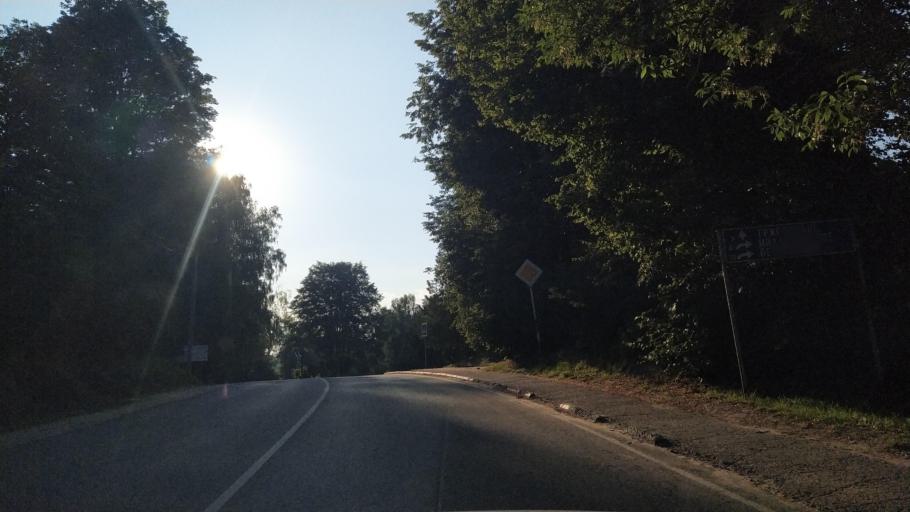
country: RU
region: Pskov
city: Pushkinskiye Gory
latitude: 57.0224
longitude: 28.9231
